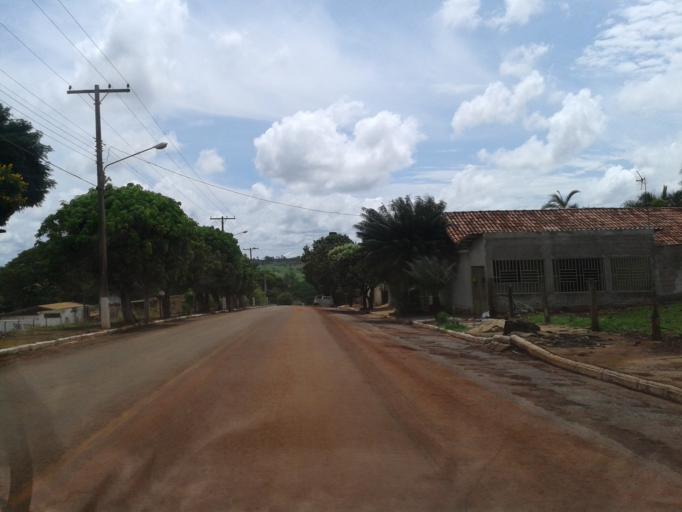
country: BR
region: Goias
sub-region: Buriti Alegre
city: Buriti Alegre
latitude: -18.1383
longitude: -49.0502
